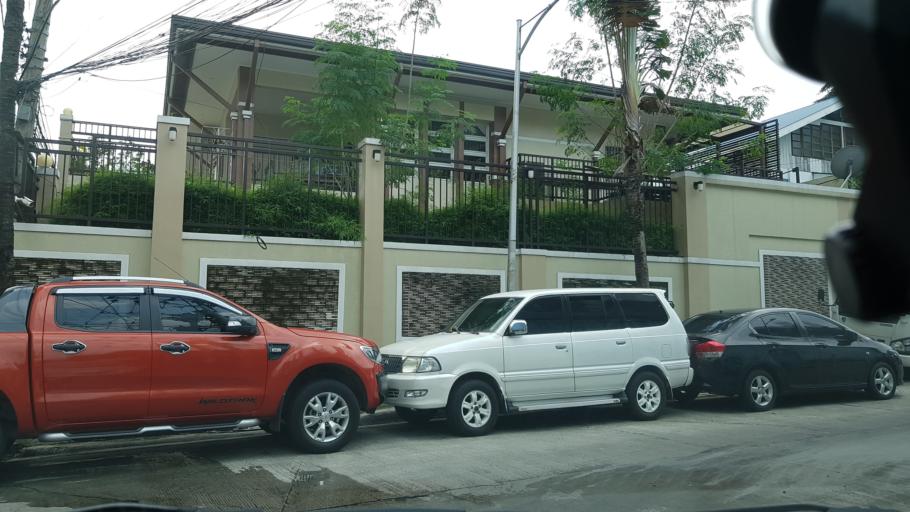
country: PH
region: Calabarzon
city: Del Monte
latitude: 14.6282
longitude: 121.0315
